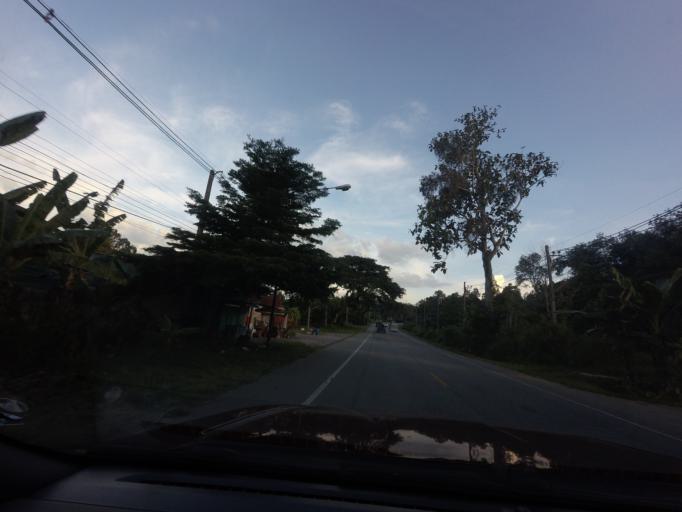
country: TH
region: Yala
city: Than To
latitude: 6.1274
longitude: 101.1921
